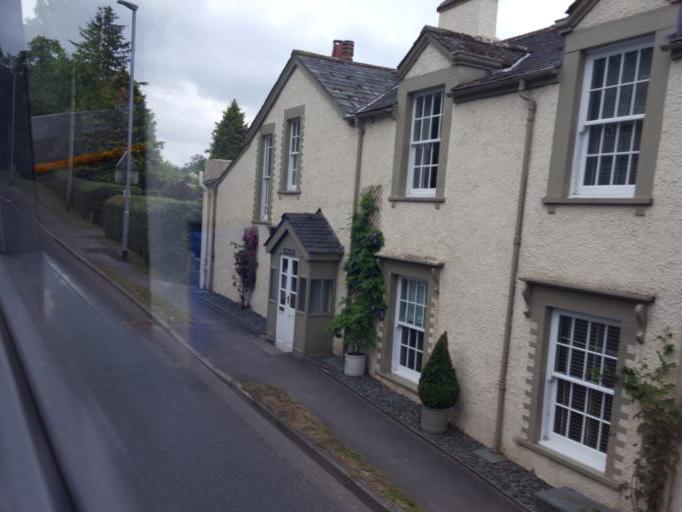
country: GB
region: England
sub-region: Cumbria
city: Keswick
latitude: 54.5999
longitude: -3.1182
